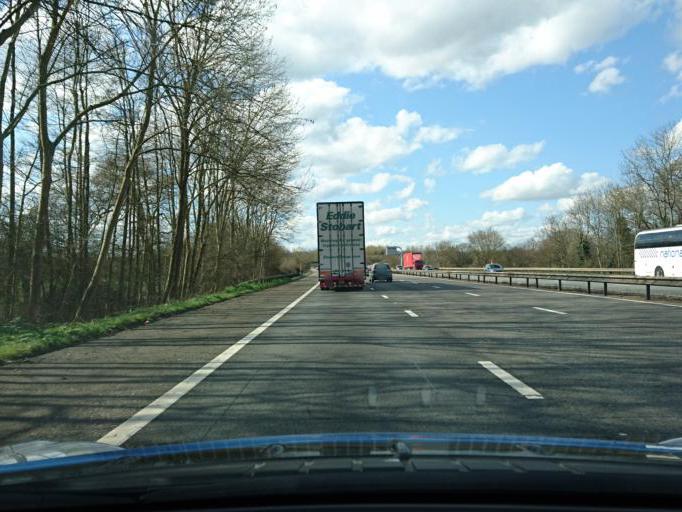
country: GB
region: England
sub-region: West Berkshire
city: Theale
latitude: 51.4547
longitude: -1.0835
